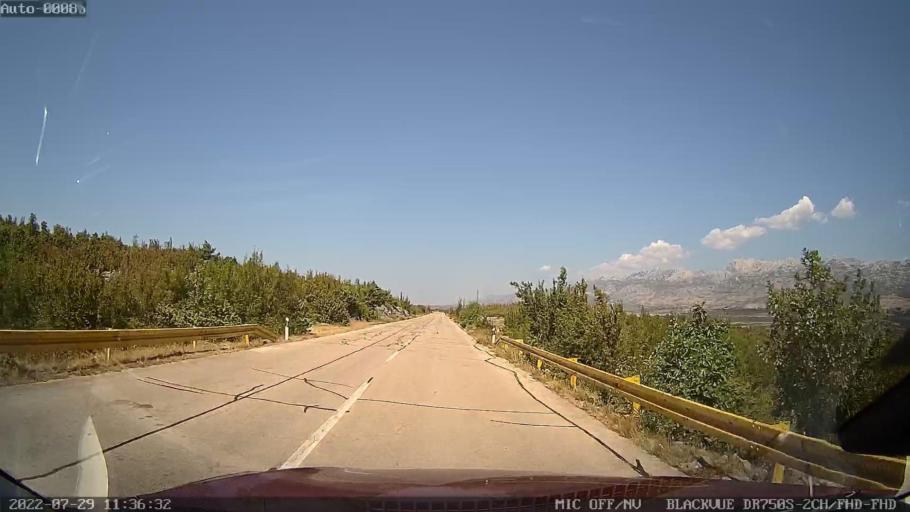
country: HR
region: Zadarska
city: Obrovac
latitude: 44.1900
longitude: 15.6967
